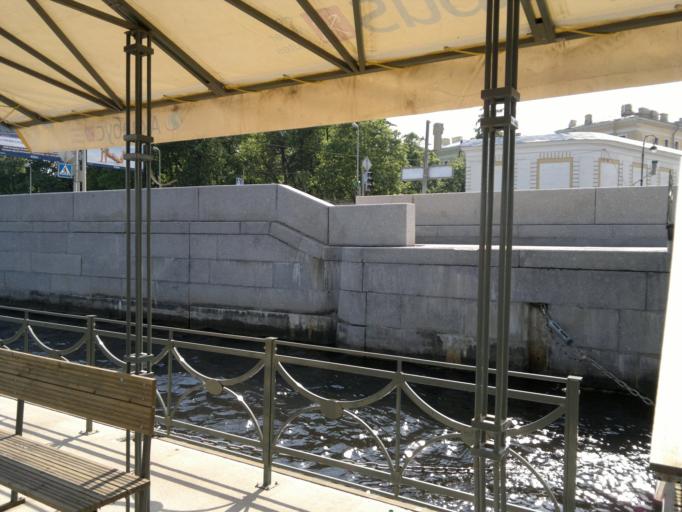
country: RU
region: Leningrad
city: Finlyandskiy
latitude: 59.9515
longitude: 30.3998
